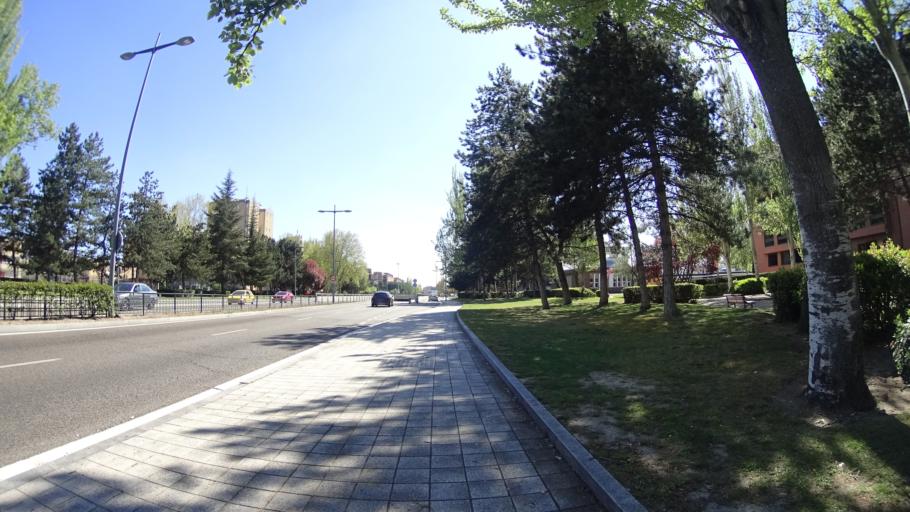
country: ES
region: Castille and Leon
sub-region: Provincia de Valladolid
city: Valladolid
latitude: 41.6499
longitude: -4.7399
